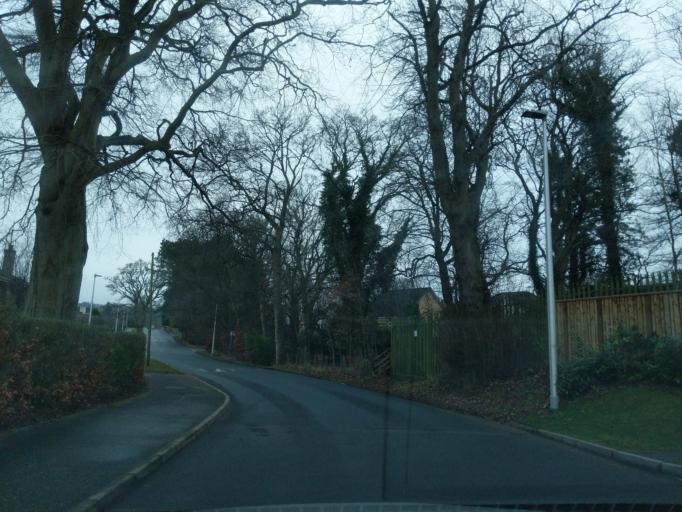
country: GB
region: Scotland
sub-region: Edinburgh
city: Balerno
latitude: 55.8915
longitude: -3.3337
